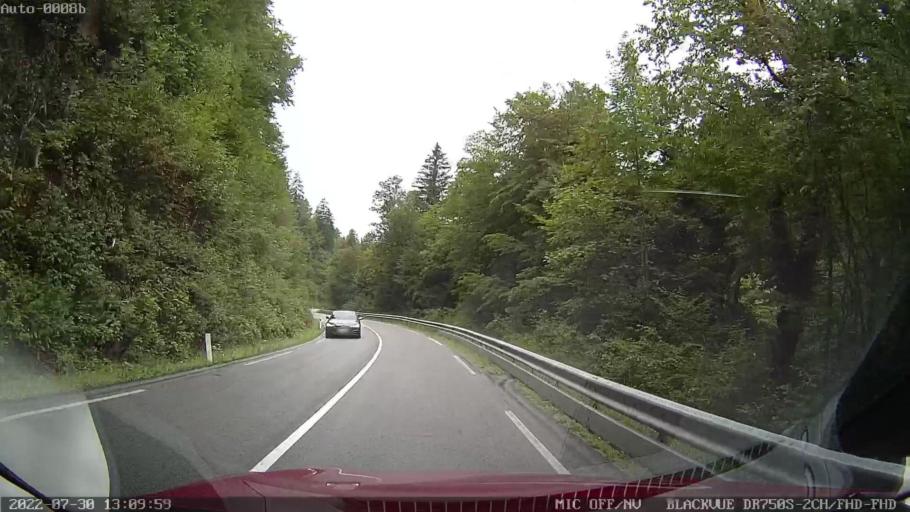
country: SI
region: Dolenjske Toplice
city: Dolenjske Toplice
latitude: 45.6910
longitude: 15.0906
